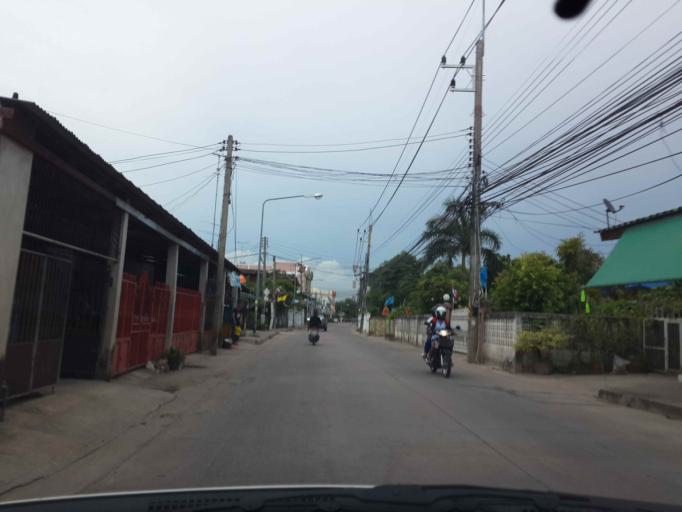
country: TH
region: Chon Buri
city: Si Racha
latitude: 13.2138
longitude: 100.9442
